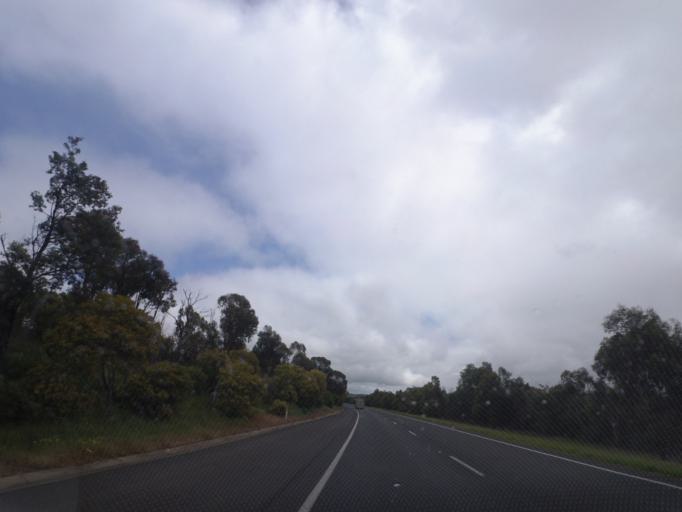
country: AU
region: Victoria
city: Black Hill
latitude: -37.5246
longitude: 143.8656
